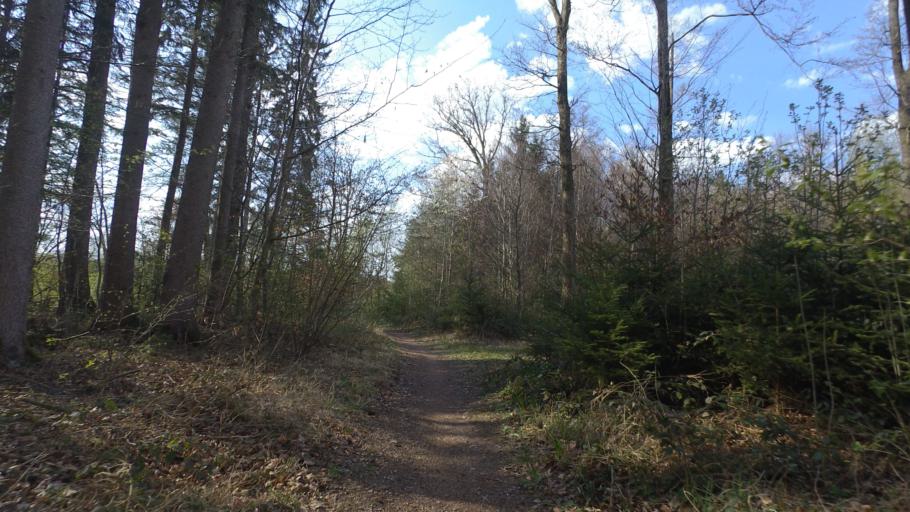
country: DE
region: Bavaria
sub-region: Upper Bavaria
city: Seeon-Seebruck
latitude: 47.9271
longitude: 12.4977
